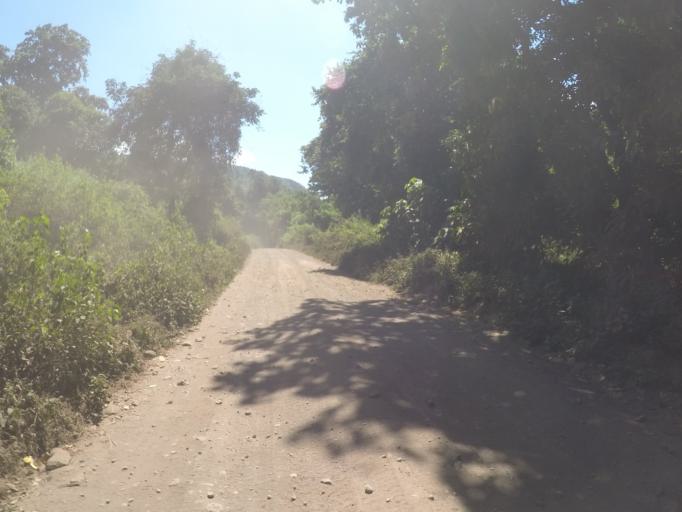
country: TZ
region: Arusha
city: Mto wa Mbu
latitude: -3.3827
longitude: 35.8287
